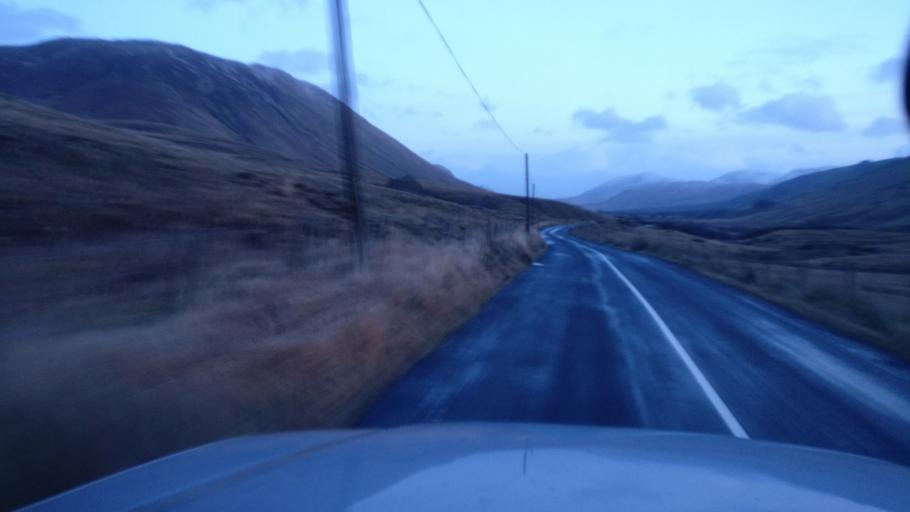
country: IE
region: Connaught
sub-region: Maigh Eo
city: Westport
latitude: 53.5756
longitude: -9.6640
